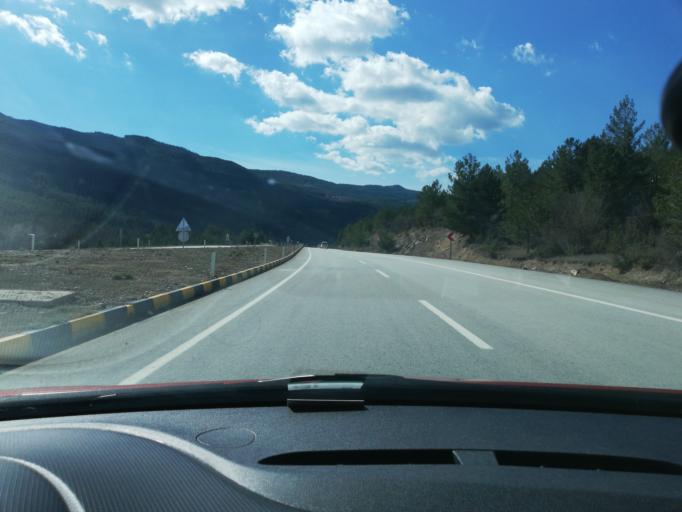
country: TR
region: Karabuk
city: Ovacik
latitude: 41.2000
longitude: 32.8429
